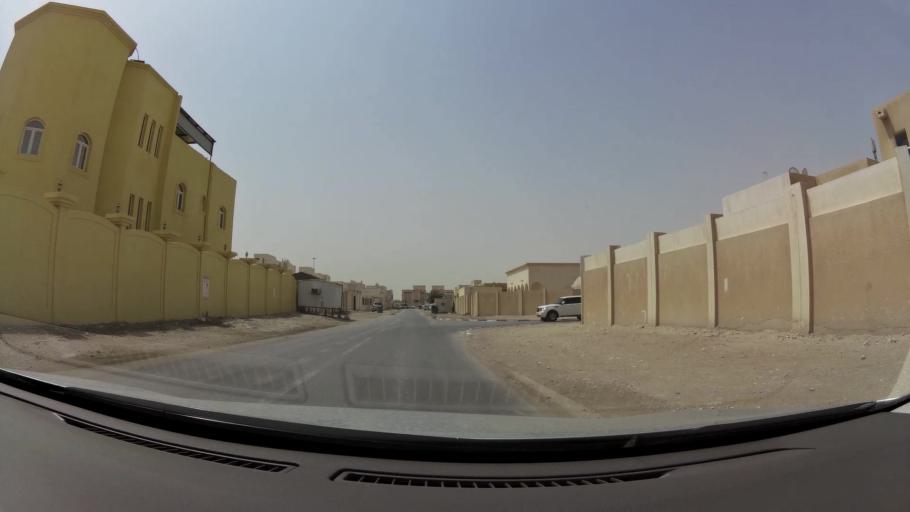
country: QA
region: Baladiyat ar Rayyan
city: Ar Rayyan
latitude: 25.2279
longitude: 51.4138
